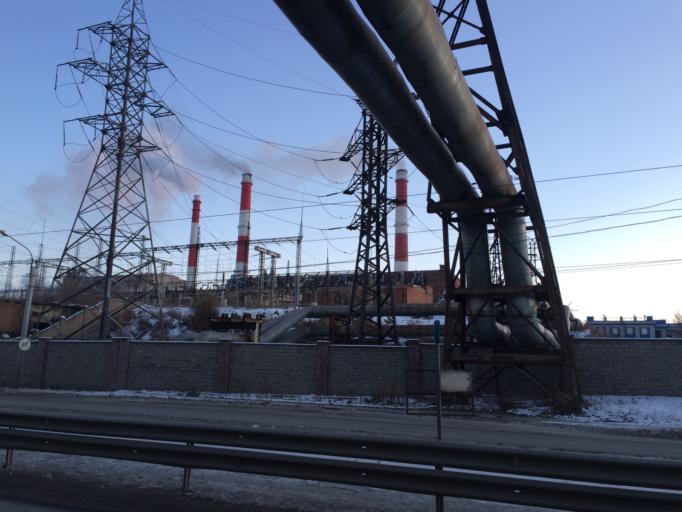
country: RU
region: Chelyabinsk
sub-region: Gorod Magnitogorsk
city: Magnitogorsk
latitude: 53.3982
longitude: 59.0172
